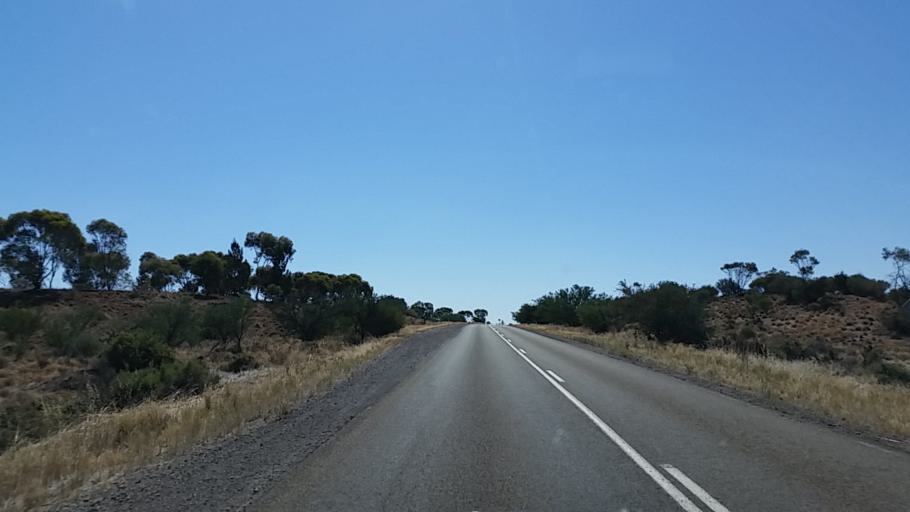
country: AU
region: South Australia
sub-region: Peterborough
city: Peterborough
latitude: -32.7200
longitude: 138.6116
